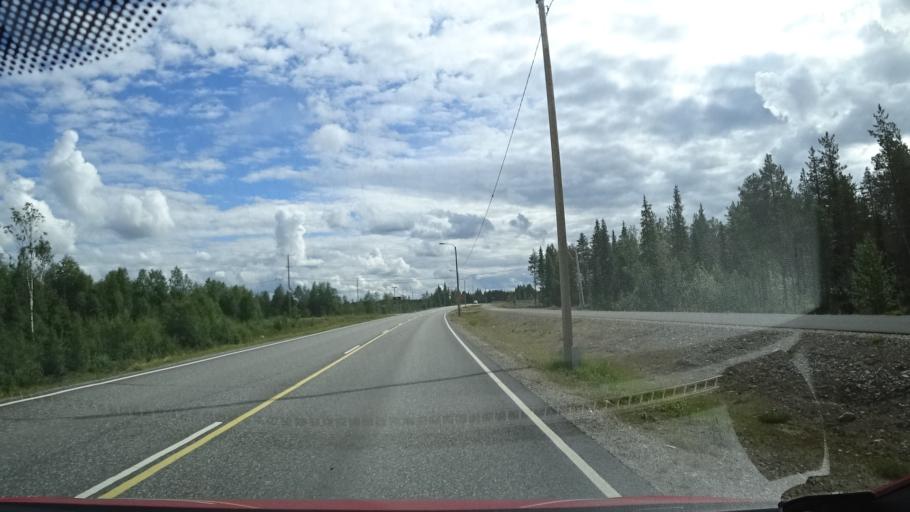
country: FI
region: Lapland
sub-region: Tunturi-Lappi
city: Kittilae
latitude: 67.4829
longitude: 24.9225
